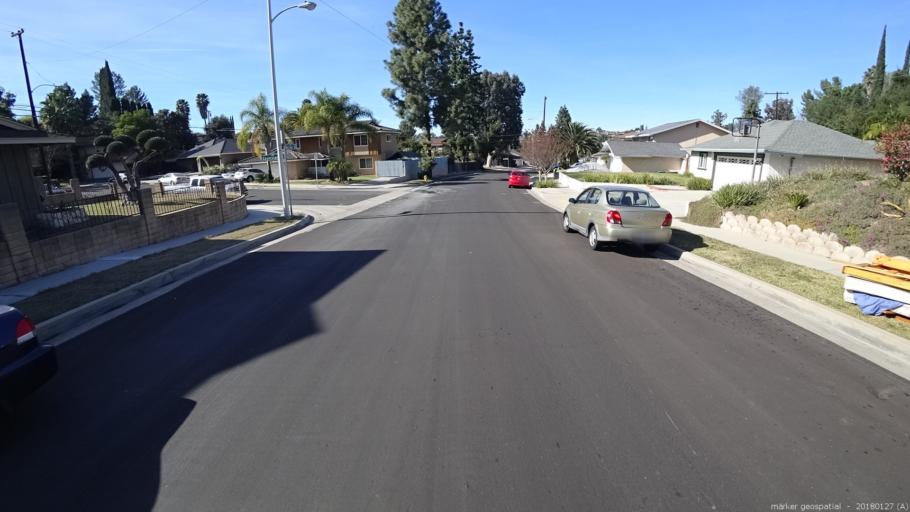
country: US
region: California
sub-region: Los Angeles County
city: Diamond Bar
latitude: 34.0228
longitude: -117.7990
